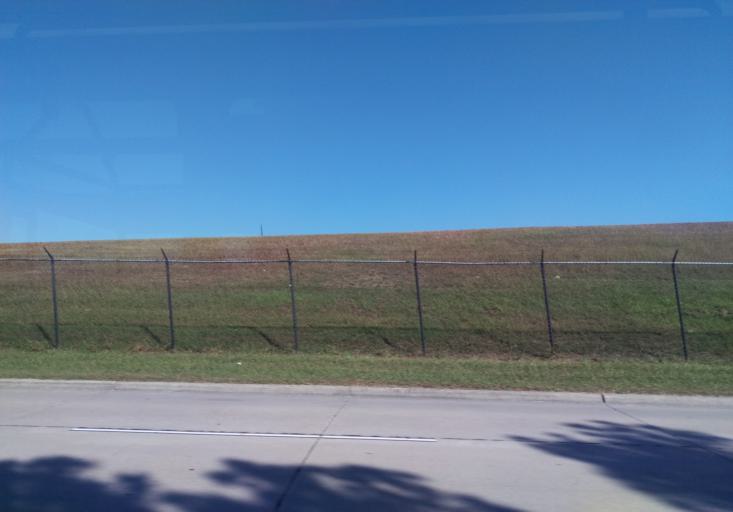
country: US
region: Texas
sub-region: Harris County
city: Aldine
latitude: 29.9814
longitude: -95.3349
